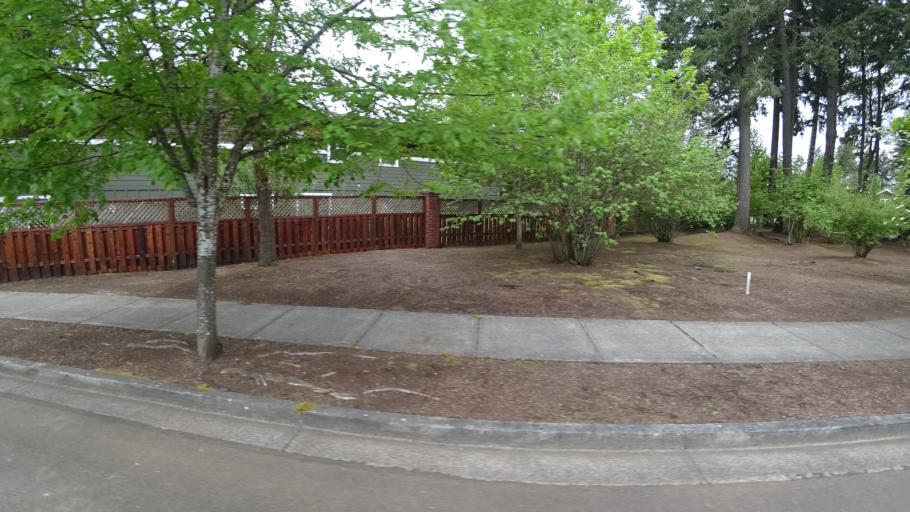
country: US
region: Oregon
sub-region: Washington County
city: Hillsboro
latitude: 45.5485
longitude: -122.9764
